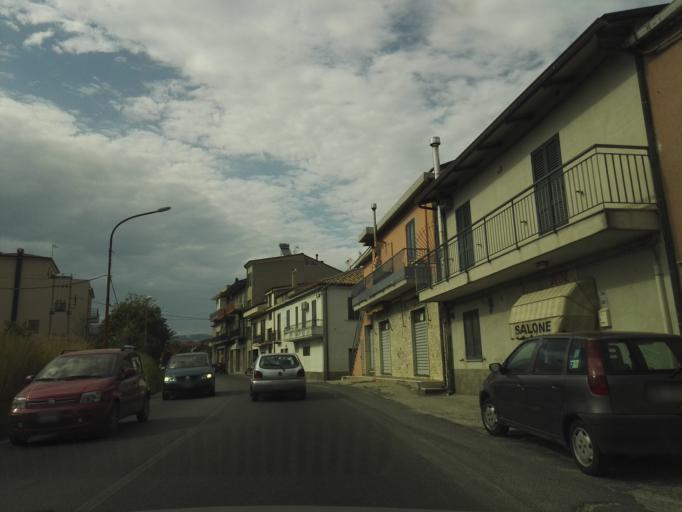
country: IT
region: Calabria
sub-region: Provincia di Catanzaro
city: Marina di Davoli
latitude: 38.6595
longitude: 16.5459
